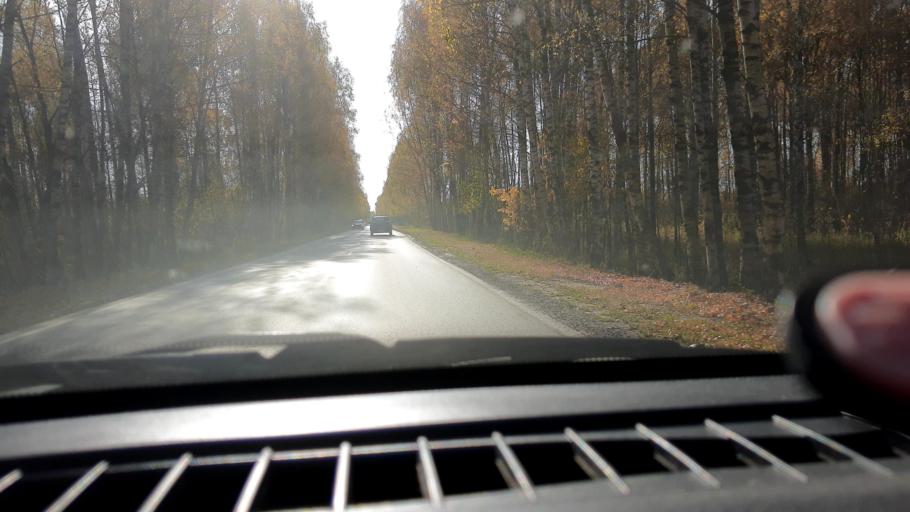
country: RU
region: Nizjnij Novgorod
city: Neklyudovo
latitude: 56.5191
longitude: 43.8370
